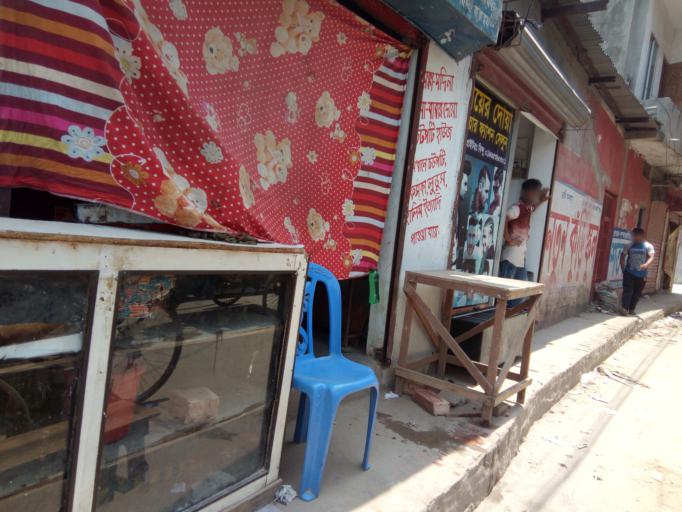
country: BD
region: Dhaka
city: Paltan
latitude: 23.7602
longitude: 90.4339
